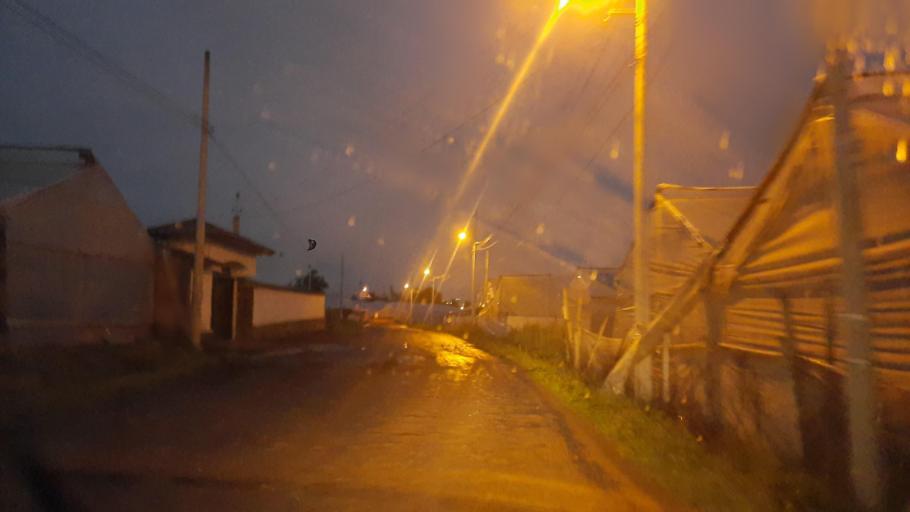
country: EC
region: Chimborazo
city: Riobamba
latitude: -1.6900
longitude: -78.6709
